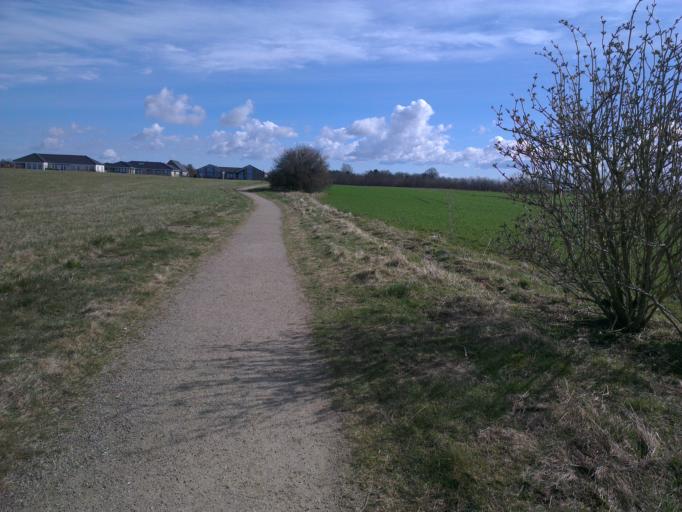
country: DK
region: Capital Region
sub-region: Frederikssund Kommune
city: Frederikssund
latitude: 55.8150
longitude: 12.0702
